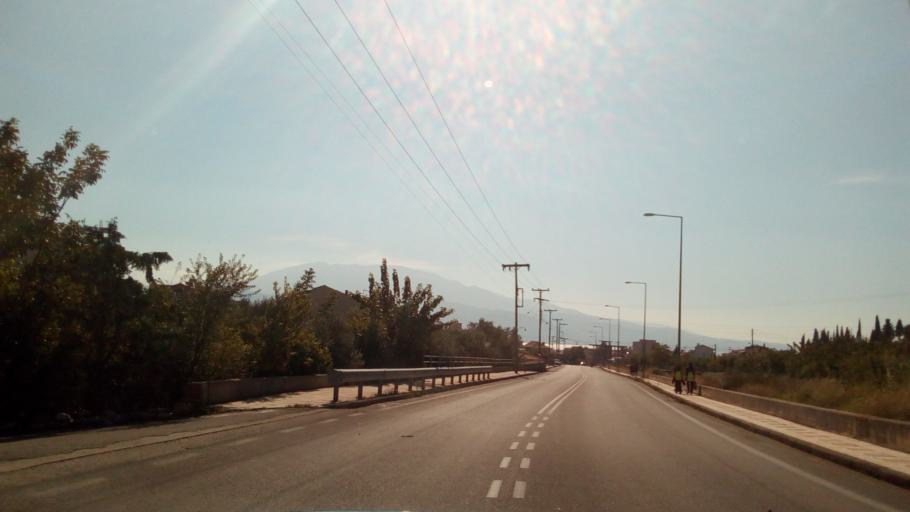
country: GR
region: West Greece
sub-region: Nomos Aitolias kai Akarnanias
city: Nafpaktos
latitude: 38.3987
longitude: 21.8435
